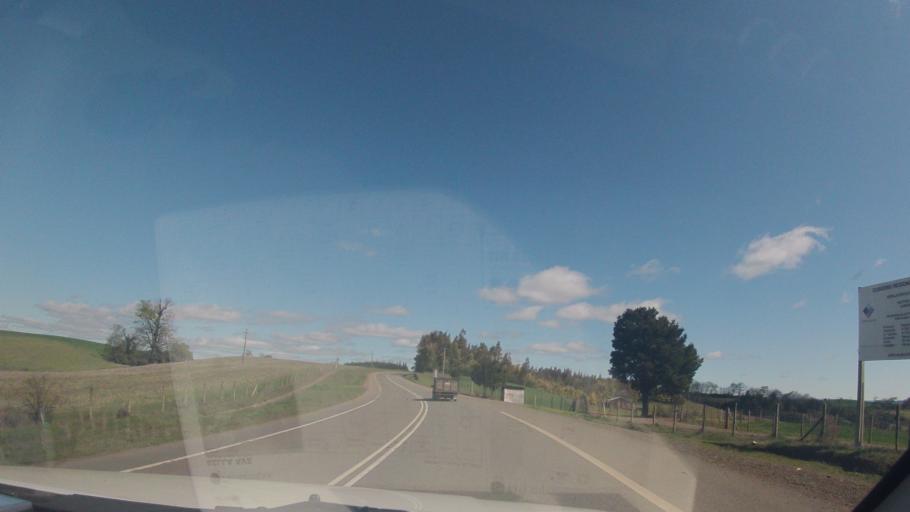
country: CL
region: Araucania
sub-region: Provincia de Malleco
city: Traiguen
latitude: -38.2022
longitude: -72.7807
